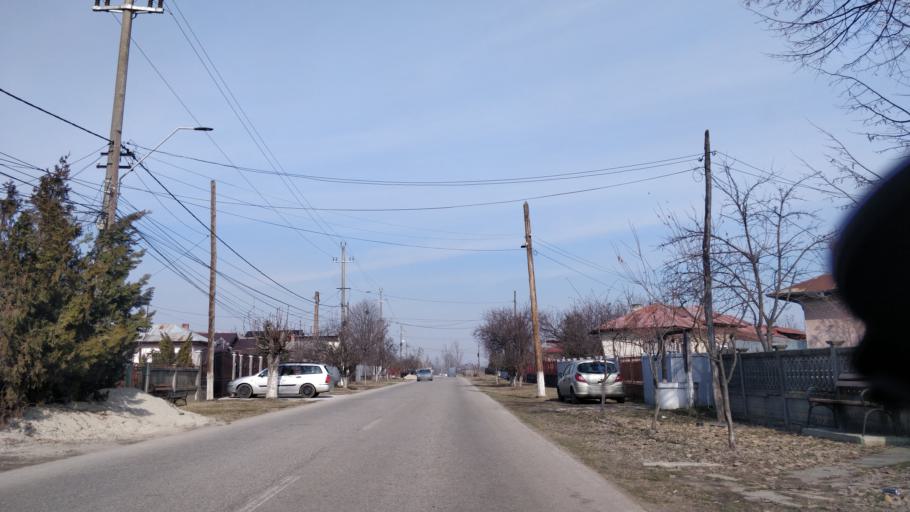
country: RO
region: Giurgiu
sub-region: Comuna Ulmi
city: Ulmi
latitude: 44.4785
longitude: 25.7698
